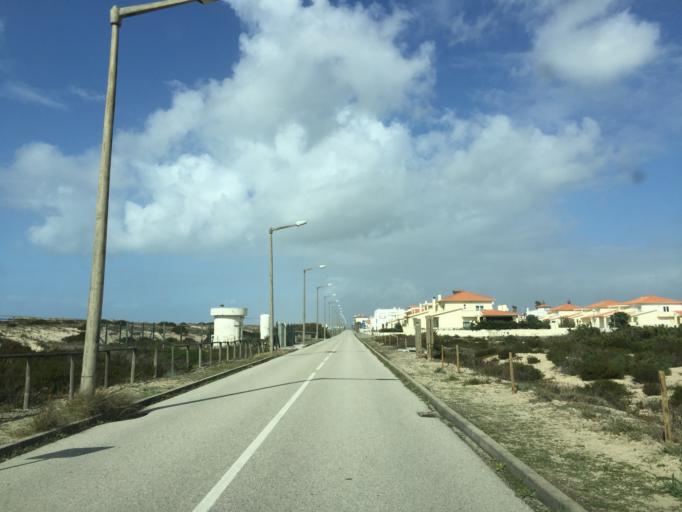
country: PT
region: Coimbra
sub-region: Figueira da Foz
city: Buarcos
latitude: 40.2113
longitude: -8.8953
